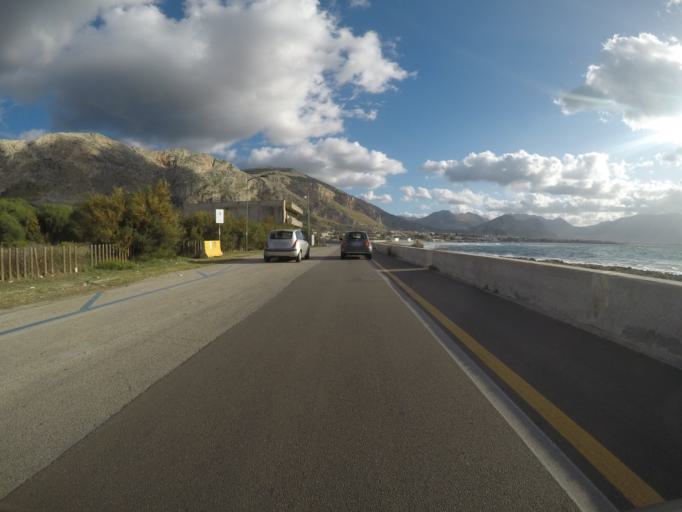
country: IT
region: Sicily
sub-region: Palermo
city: Isola delle Femmine
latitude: 38.1951
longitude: 13.2438
